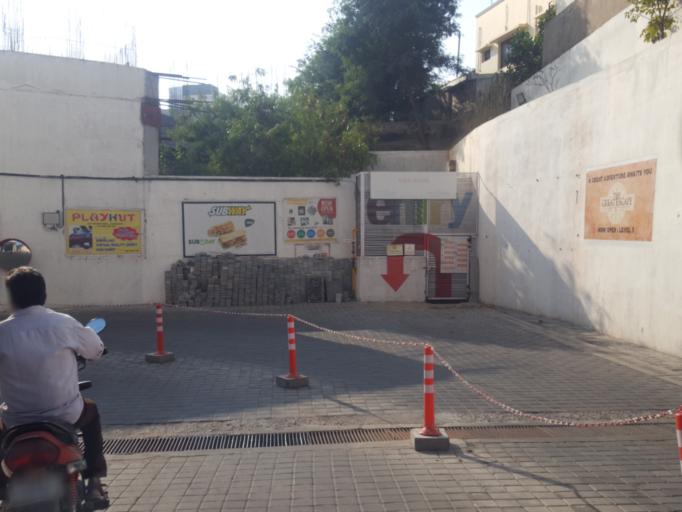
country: IN
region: Telangana
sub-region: Rangareddi
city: Kukatpalli
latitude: 17.4520
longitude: 78.3624
